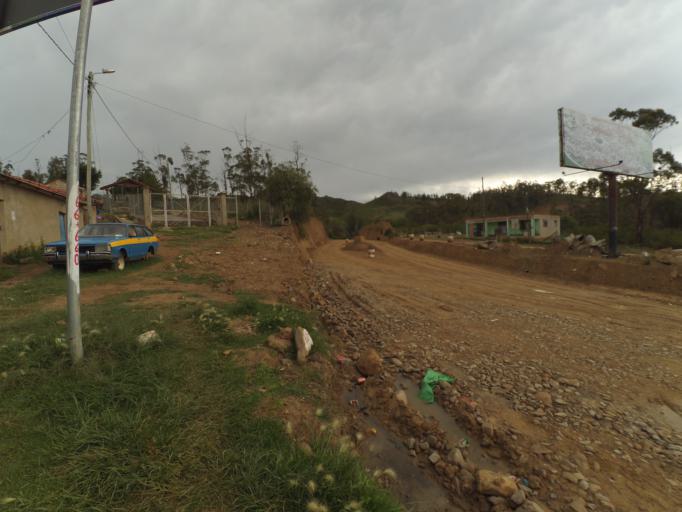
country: BO
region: Chuquisaca
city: Padilla
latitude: -19.3137
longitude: -64.3074
